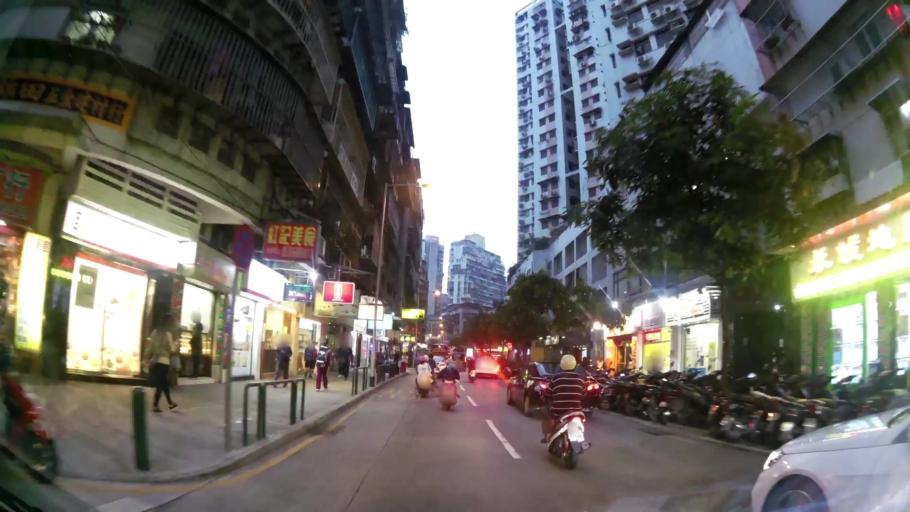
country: MO
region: Macau
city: Macau
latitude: 22.2078
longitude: 113.5499
